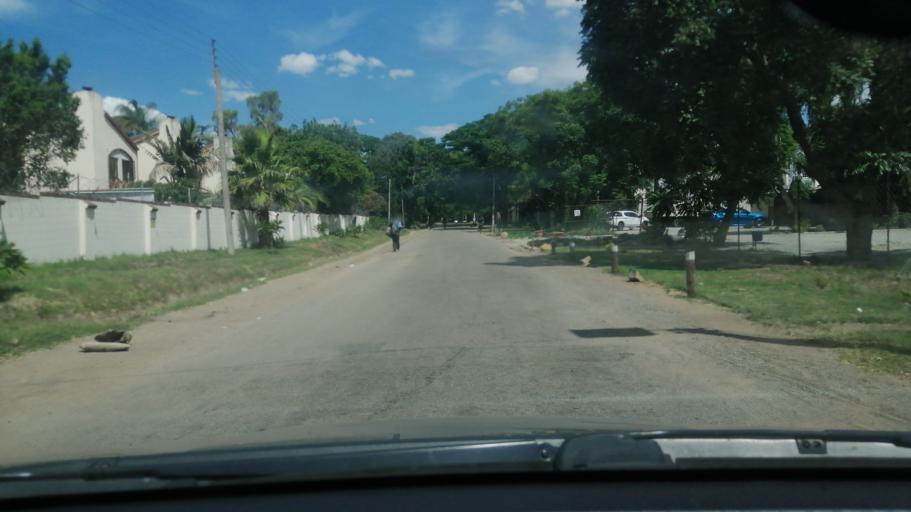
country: ZW
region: Harare
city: Harare
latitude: -17.8110
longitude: 31.0757
